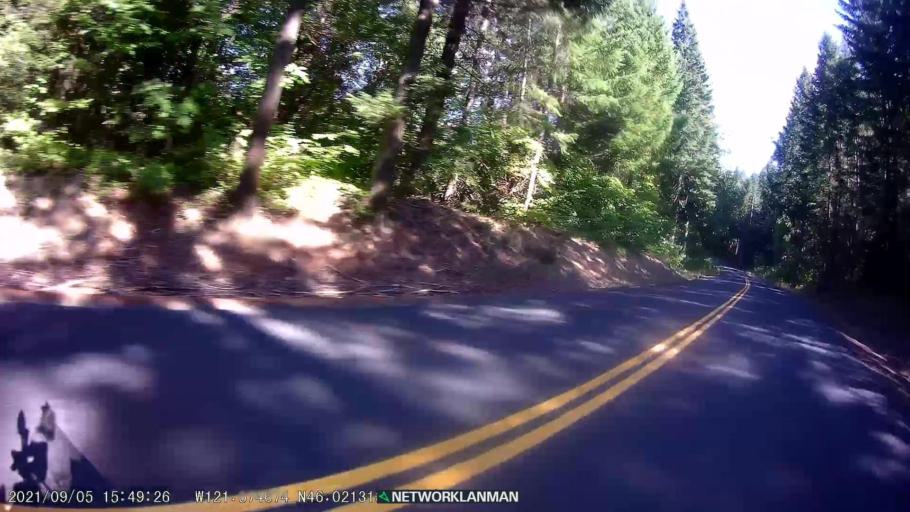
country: US
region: Washington
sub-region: Klickitat County
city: White Salmon
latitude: 46.0212
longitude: -121.5746
